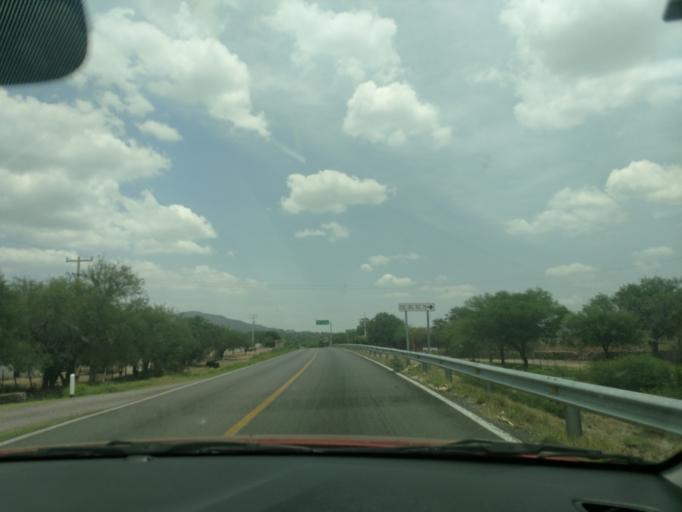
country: MX
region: San Luis Potosi
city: Villa Juarez
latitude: 22.0185
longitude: -100.3878
